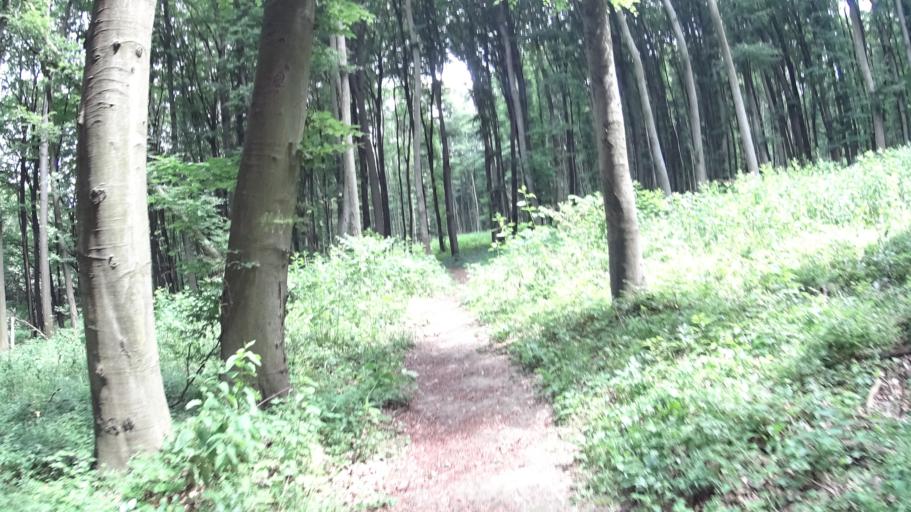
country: HU
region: Pest
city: Nagymaros
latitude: 47.8005
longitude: 18.9337
